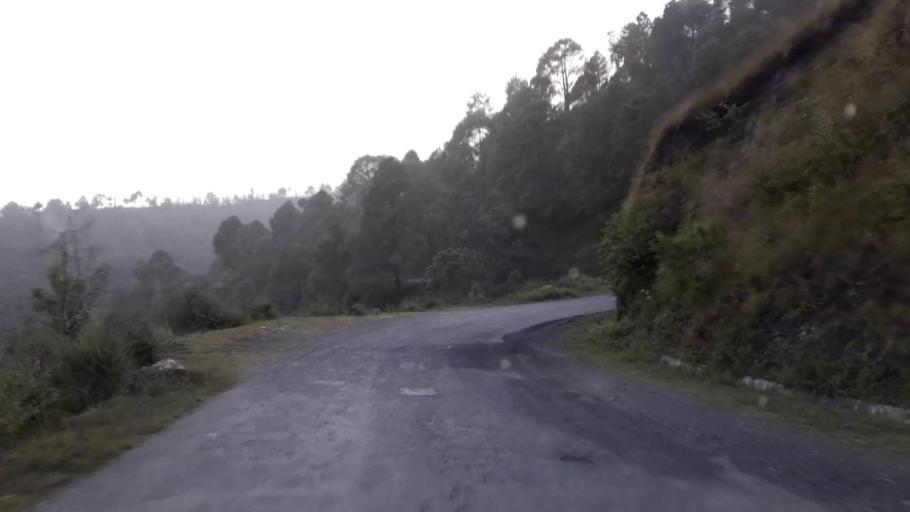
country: IN
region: Himachal Pradesh
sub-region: Shimla
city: Shimla
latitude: 31.0523
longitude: 77.1558
